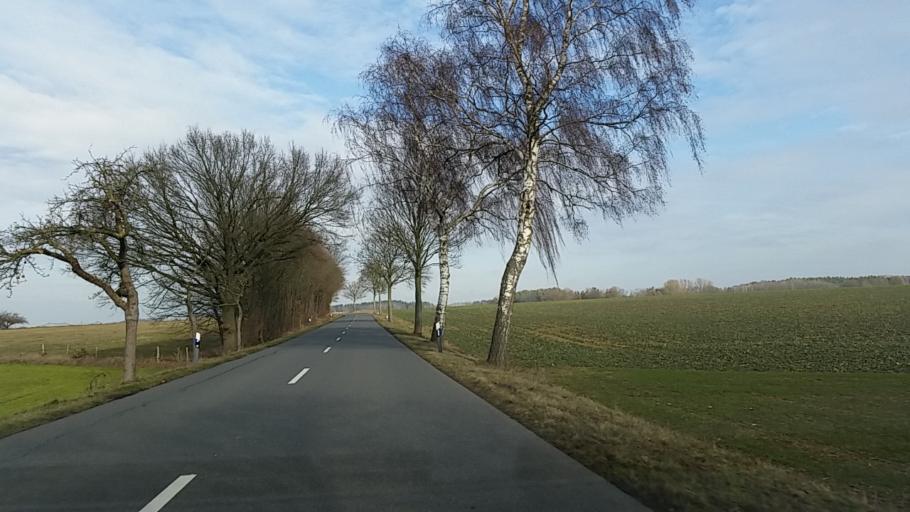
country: DE
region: Lower Saxony
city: Altenmedingen
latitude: 53.1555
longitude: 10.6200
